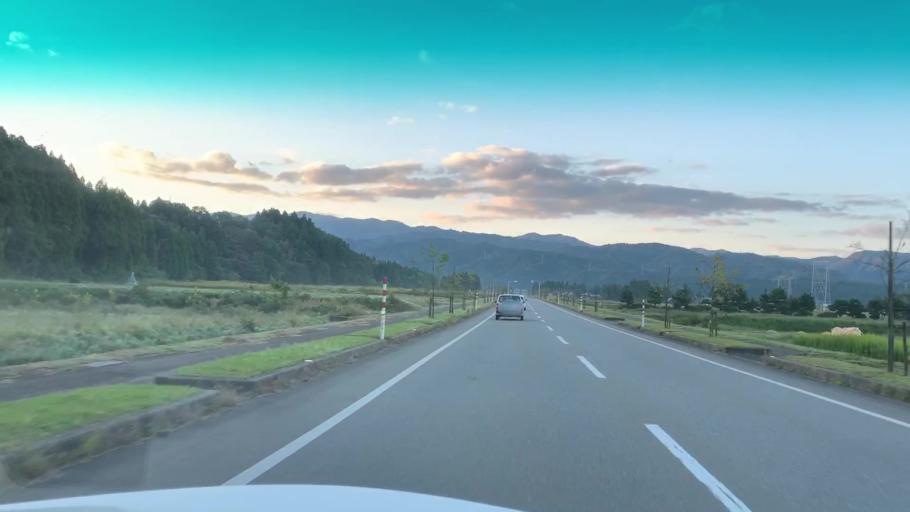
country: JP
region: Toyama
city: Kamiichi
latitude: 36.6044
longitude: 137.3259
